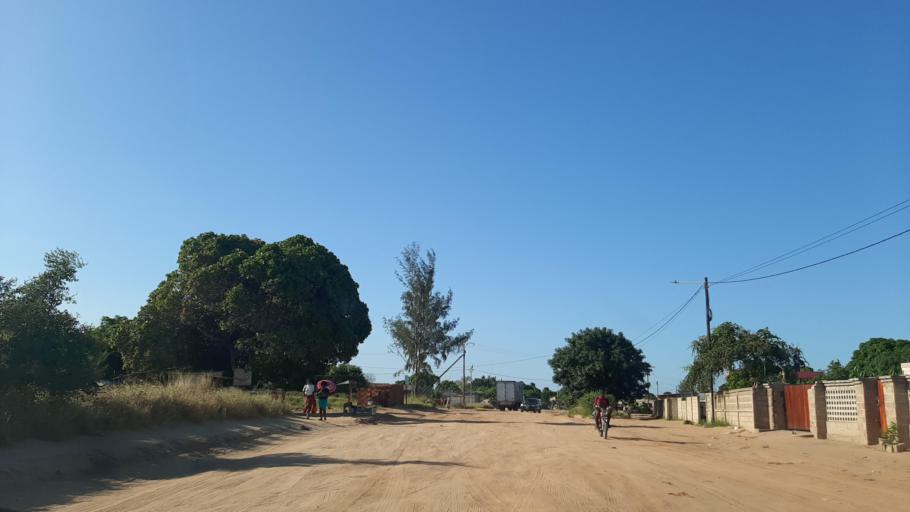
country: MZ
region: Maputo City
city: Maputo
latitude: -25.8044
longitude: 32.5470
